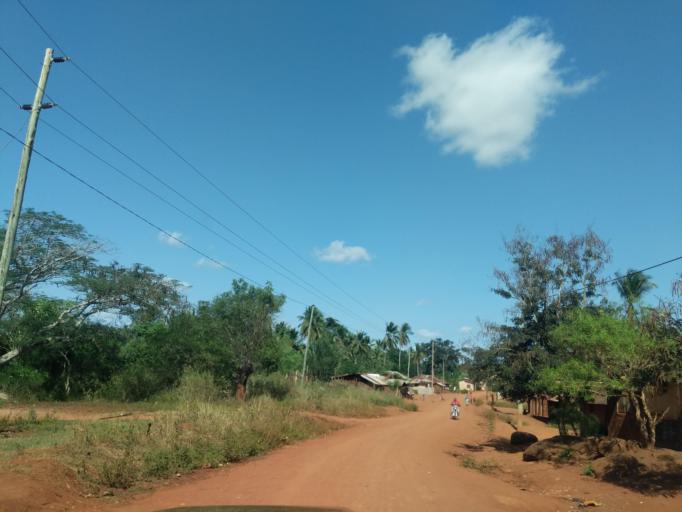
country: TZ
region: Tanga
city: Muheza
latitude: -5.3852
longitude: 38.5787
